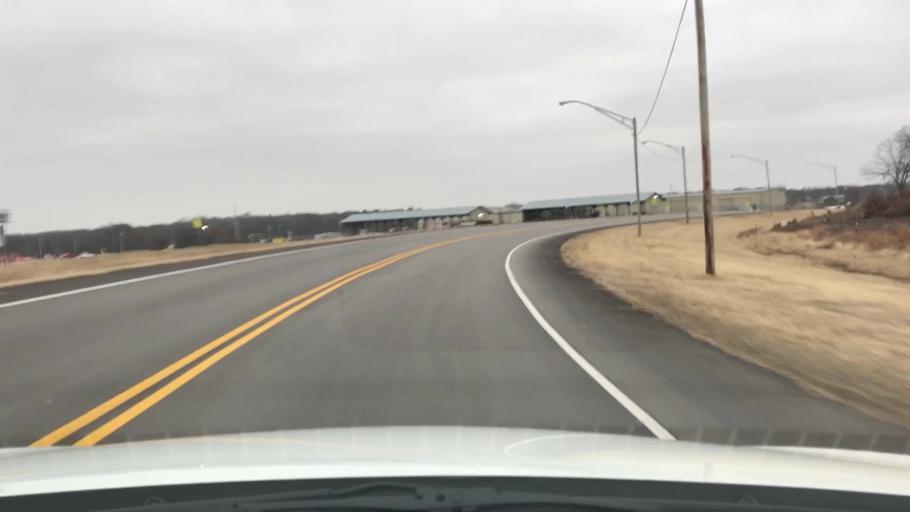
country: US
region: Oklahoma
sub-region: Carter County
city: Ardmore
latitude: 34.1754
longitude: -97.1699
